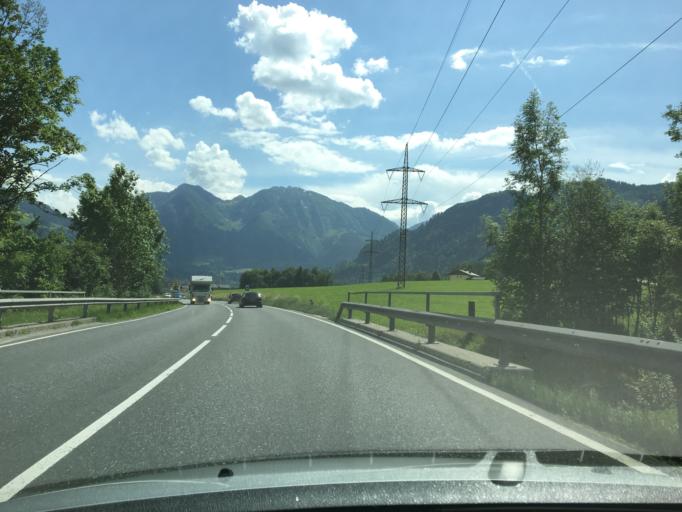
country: AT
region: Salzburg
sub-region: Politischer Bezirk Sankt Johann im Pongau
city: Sankt Johann im Pongau
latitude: 47.3624
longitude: 13.2008
